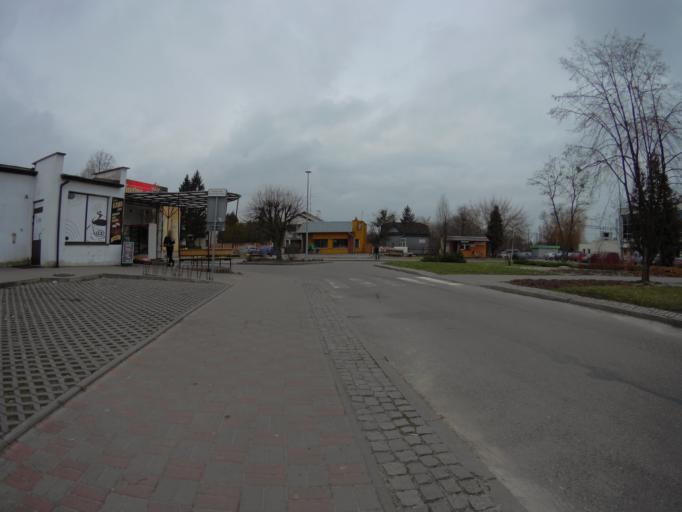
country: PL
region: Lublin Voivodeship
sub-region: Powiat bialski
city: Terespol
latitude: 52.0732
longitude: 23.6041
